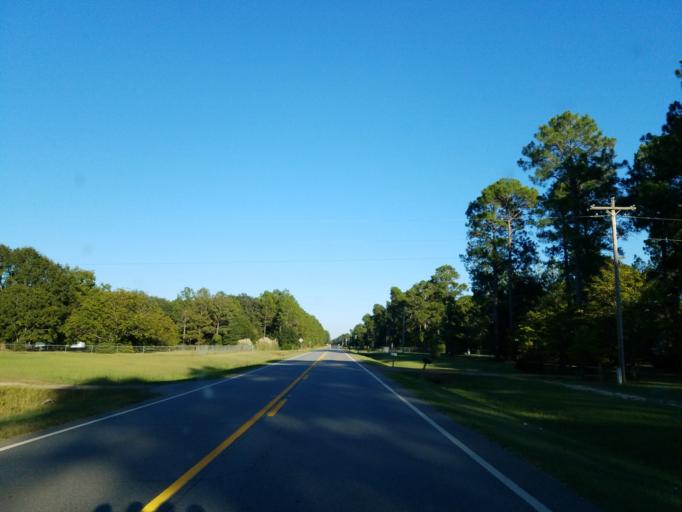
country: US
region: Georgia
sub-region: Lee County
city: Leesburg
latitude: 31.7272
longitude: -84.0552
